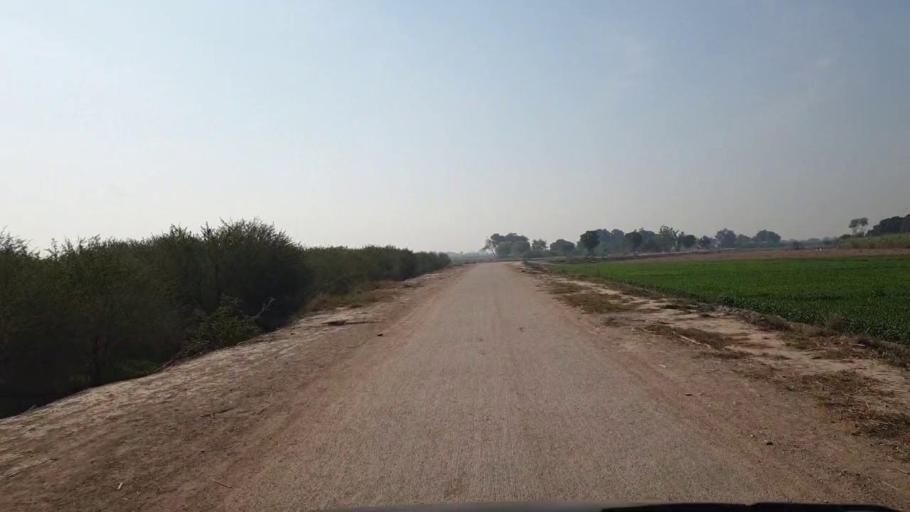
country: PK
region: Sindh
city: Tando Allahyar
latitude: 25.4150
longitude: 68.7436
